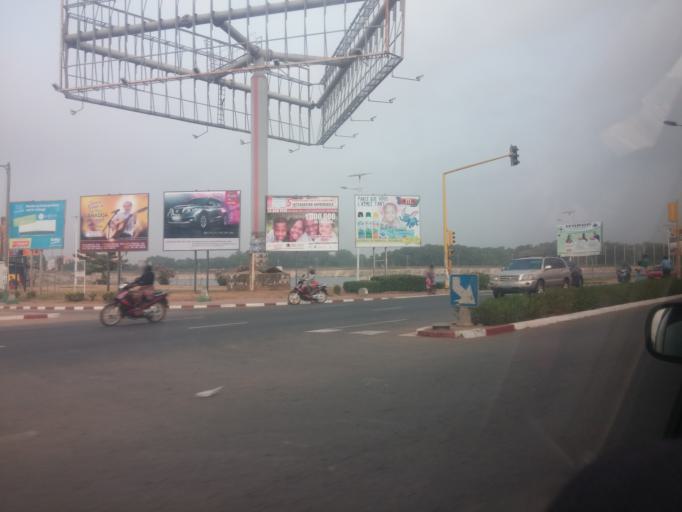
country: TG
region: Maritime
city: Lome
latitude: 6.1652
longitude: 1.2228
